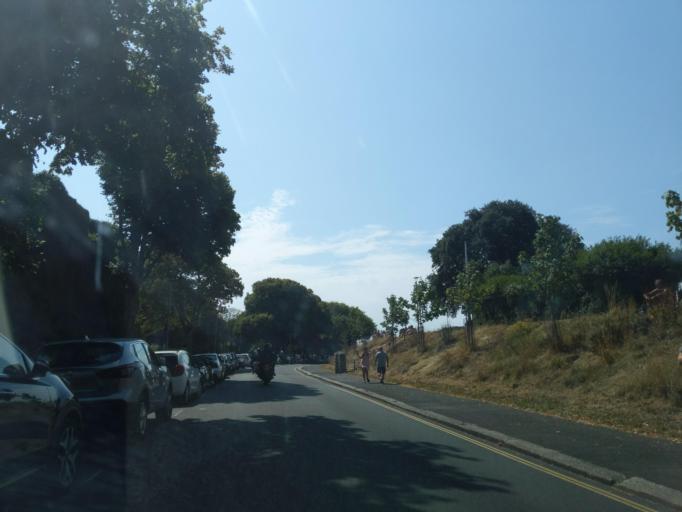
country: GB
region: England
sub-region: Plymouth
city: Plymouth
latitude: 50.3660
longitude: -4.1394
